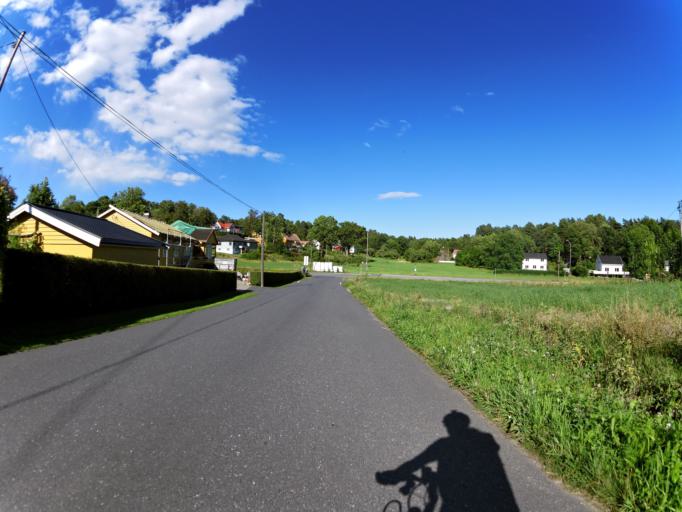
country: NO
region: Ostfold
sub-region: Fredrikstad
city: Fredrikstad
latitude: 59.1745
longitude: 10.8446
